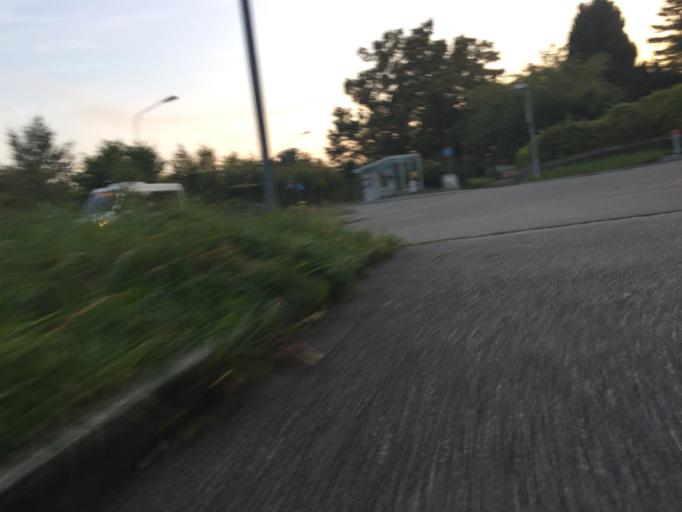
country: CH
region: Zurich
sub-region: Bezirk Zuerich
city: Zuerich (Kreis 7)
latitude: 47.3849
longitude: 8.5773
